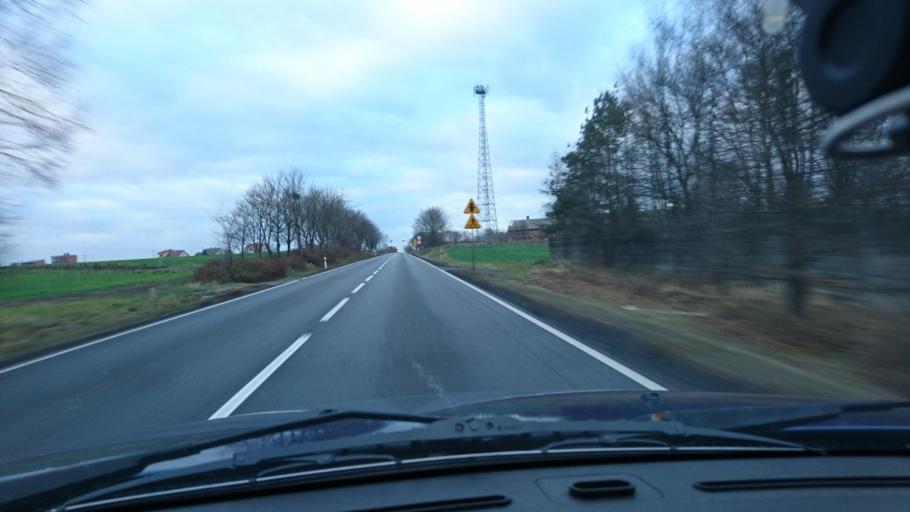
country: PL
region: Greater Poland Voivodeship
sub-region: Powiat kepinski
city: Opatow
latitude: 51.2115
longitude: 18.1443
